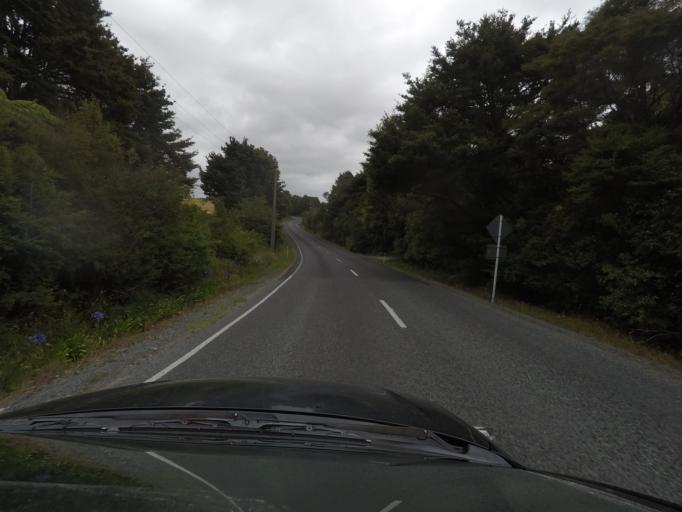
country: NZ
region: Auckland
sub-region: Auckland
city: Wellsford
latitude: -36.2803
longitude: 174.5896
